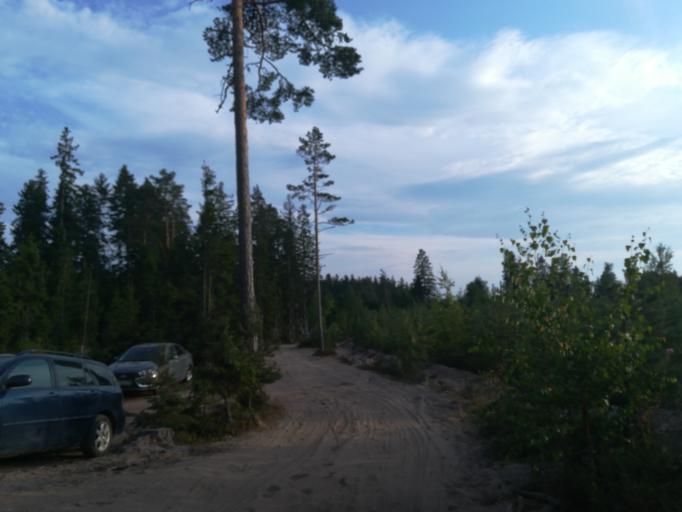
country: RU
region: Leningrad
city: Ust'-Luga
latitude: 59.6787
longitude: 28.2279
